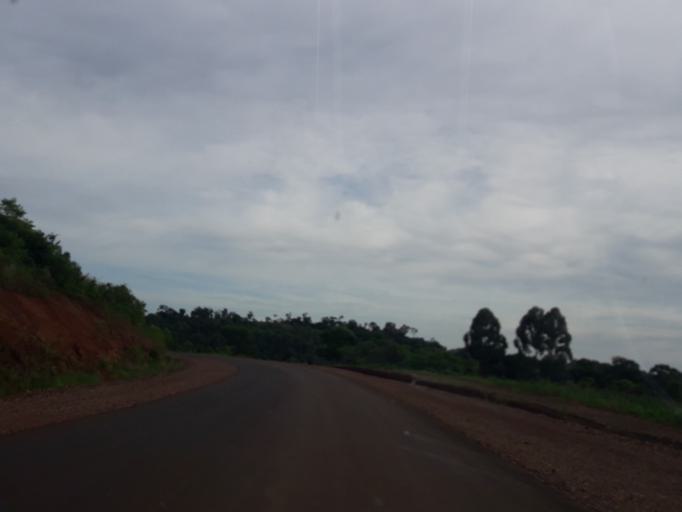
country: AR
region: Misiones
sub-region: Departamento de San Pedro
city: San Pedro
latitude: -26.5310
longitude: -53.9396
